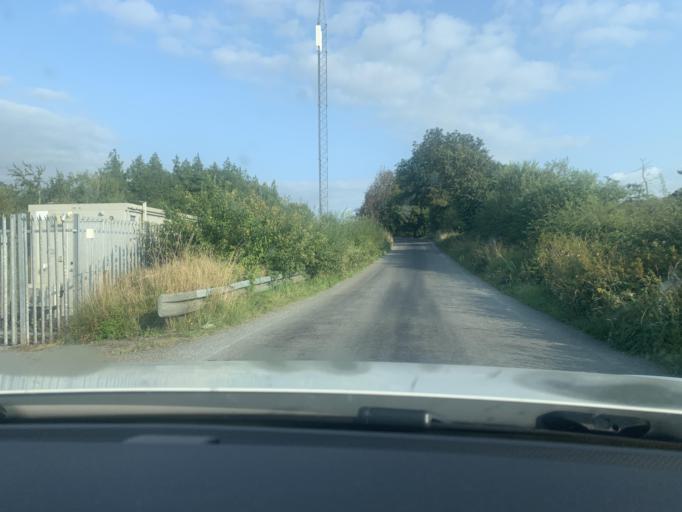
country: IE
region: Connaught
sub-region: Roscommon
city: Boyle
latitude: 53.9560
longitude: -8.2088
